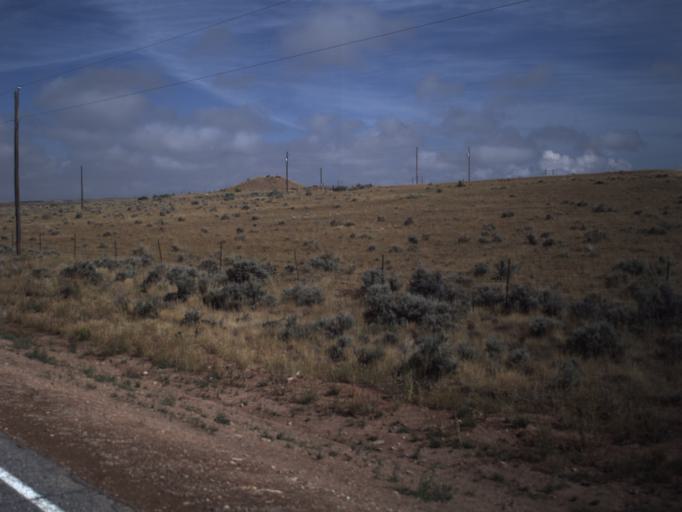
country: US
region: Wyoming
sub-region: Uinta County
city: Evanston
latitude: 41.4223
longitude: -111.0516
